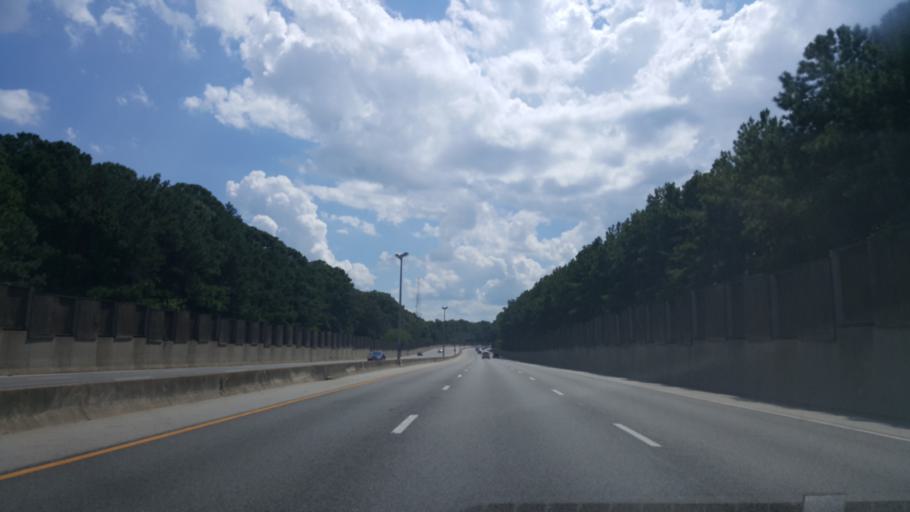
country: US
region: Virginia
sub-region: City of Hampton
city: Hampton
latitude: 37.0241
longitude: -76.3805
